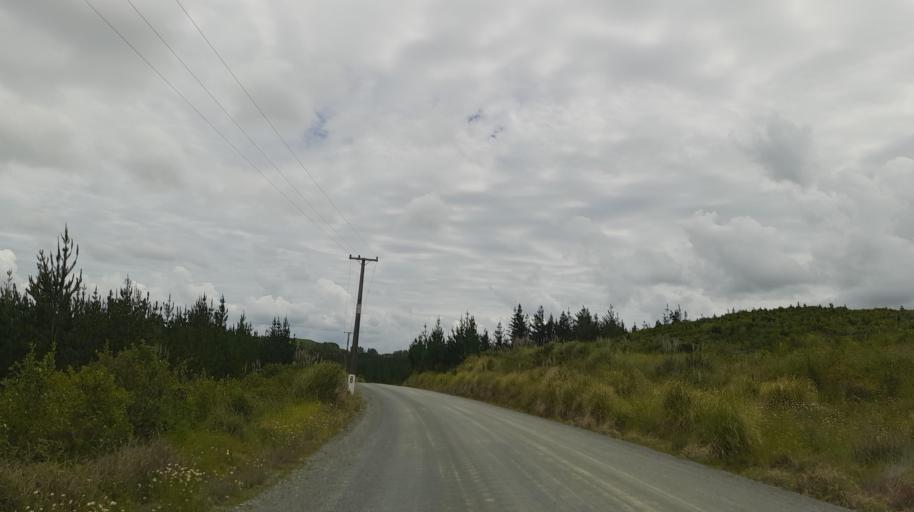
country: NZ
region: Auckland
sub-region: Auckland
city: Wellsford
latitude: -36.2309
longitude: 174.4445
